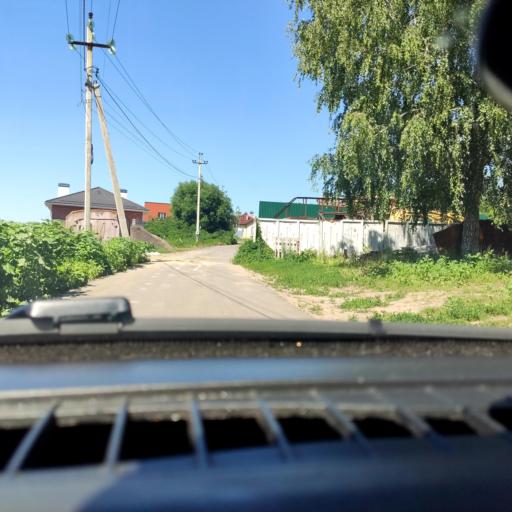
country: RU
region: Voronezj
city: Podgornoye
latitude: 51.7917
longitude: 39.1350
